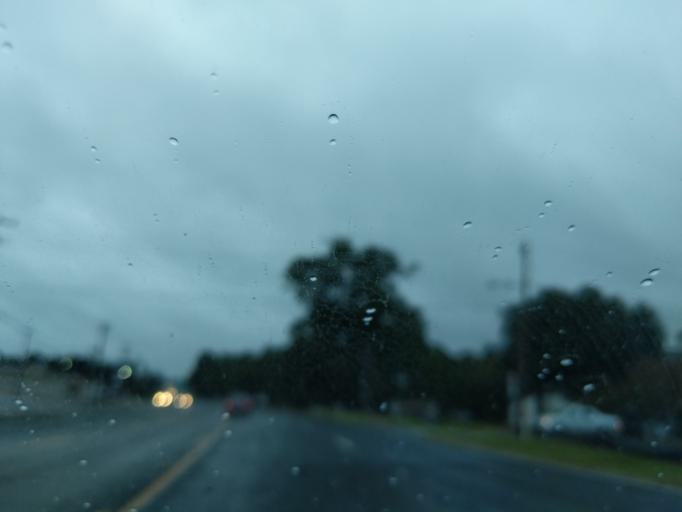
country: US
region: Texas
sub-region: Nacogdoches County
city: Nacogdoches
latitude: 31.6409
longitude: -94.6536
